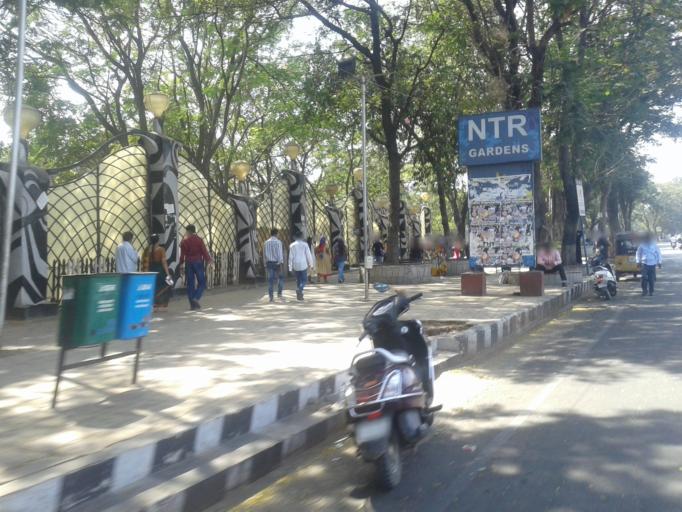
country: IN
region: Telangana
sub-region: Hyderabad
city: Hyderabad
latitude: 17.4141
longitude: 78.4691
